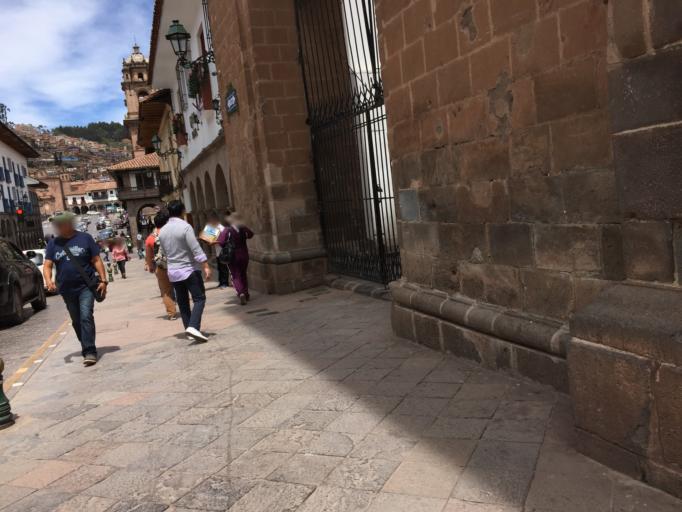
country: PE
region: Cusco
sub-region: Provincia de Cusco
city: Cusco
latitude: -13.5179
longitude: -71.9793
